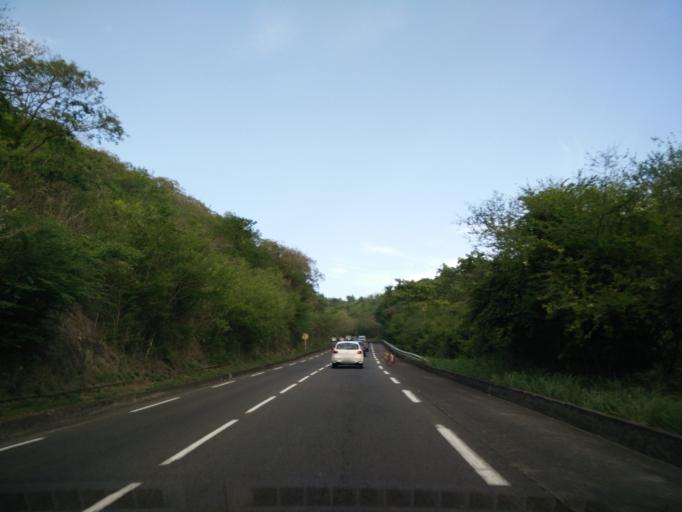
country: MQ
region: Martinique
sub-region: Martinique
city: Fort-de-France
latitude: 14.6562
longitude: -61.1471
